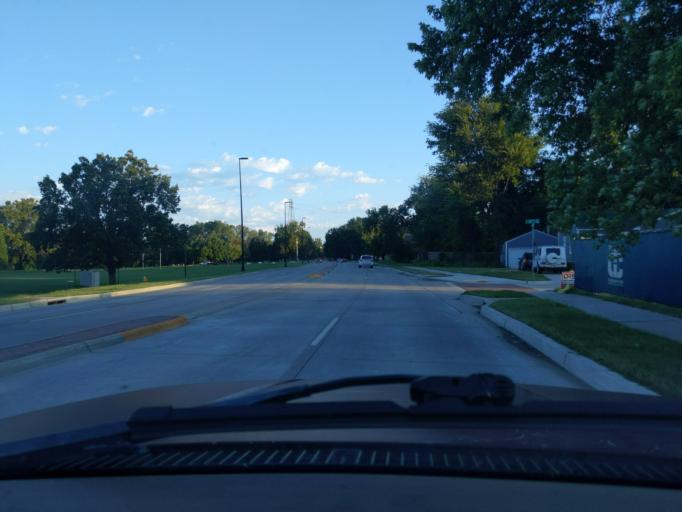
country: US
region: Oklahoma
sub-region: Tulsa County
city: Tulsa
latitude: 36.1081
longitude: -95.9828
